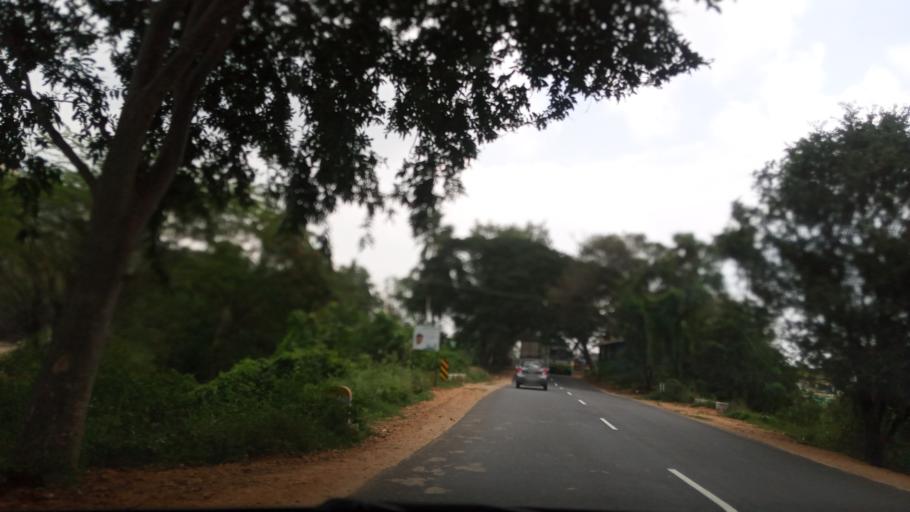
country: IN
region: Andhra Pradesh
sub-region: Chittoor
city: Madanapalle
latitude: 13.6365
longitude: 78.5863
